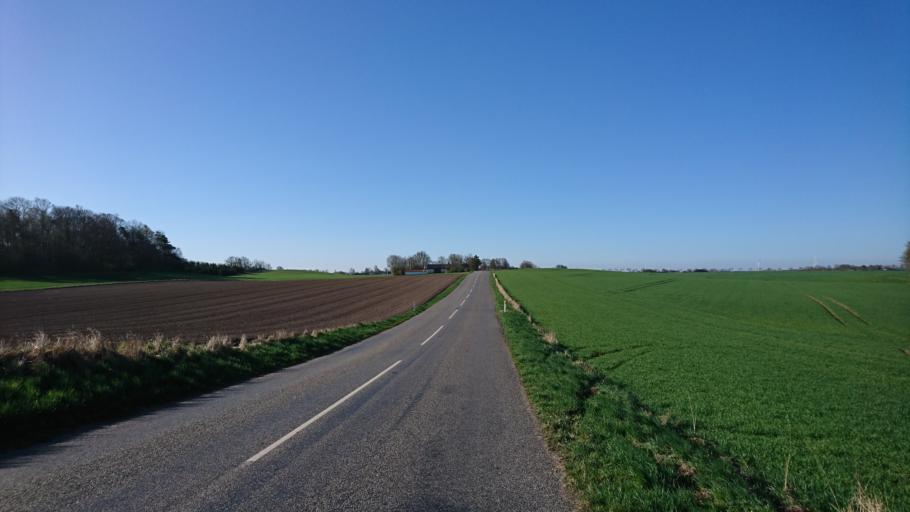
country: DK
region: Capital Region
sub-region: Frederikssund Kommune
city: Skibby
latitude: 55.7360
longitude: 11.9291
